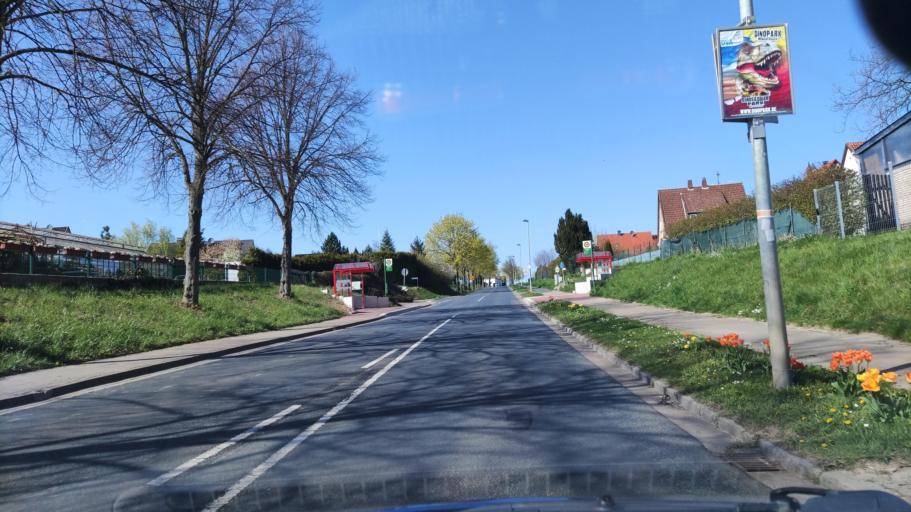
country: DE
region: Lower Saxony
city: Nordstemmen
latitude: 52.1454
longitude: 9.7755
